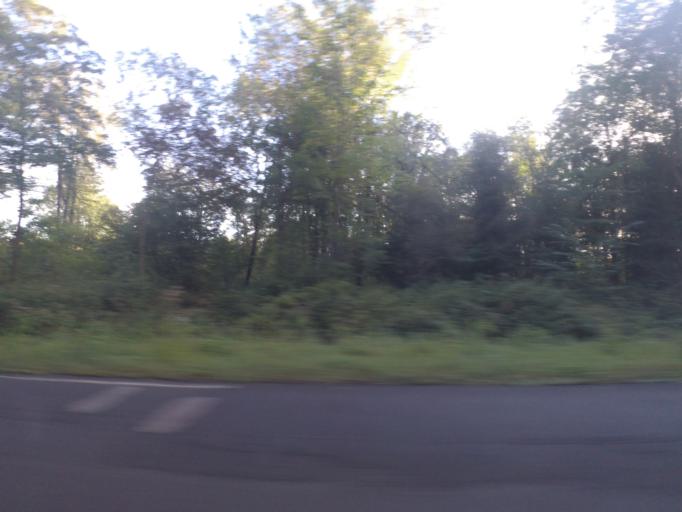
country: DE
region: Hesse
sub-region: Regierungsbezirk Darmstadt
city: Bad Soden-Salmunster
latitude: 50.3225
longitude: 9.3635
